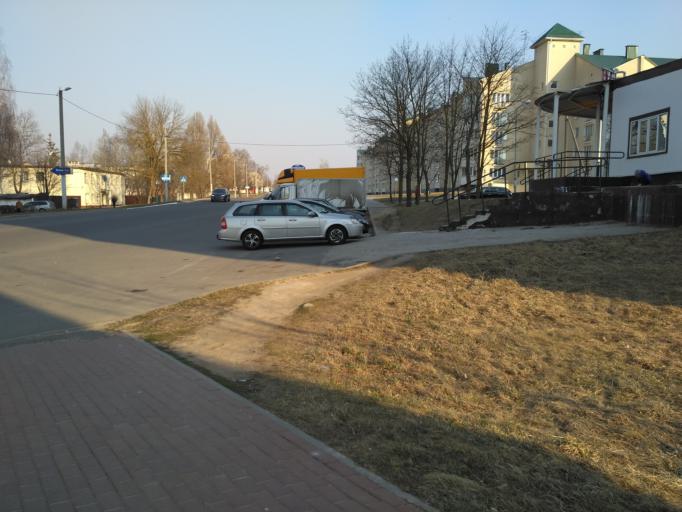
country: BY
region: Minsk
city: Zaslawye
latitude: 54.0133
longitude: 27.2605
